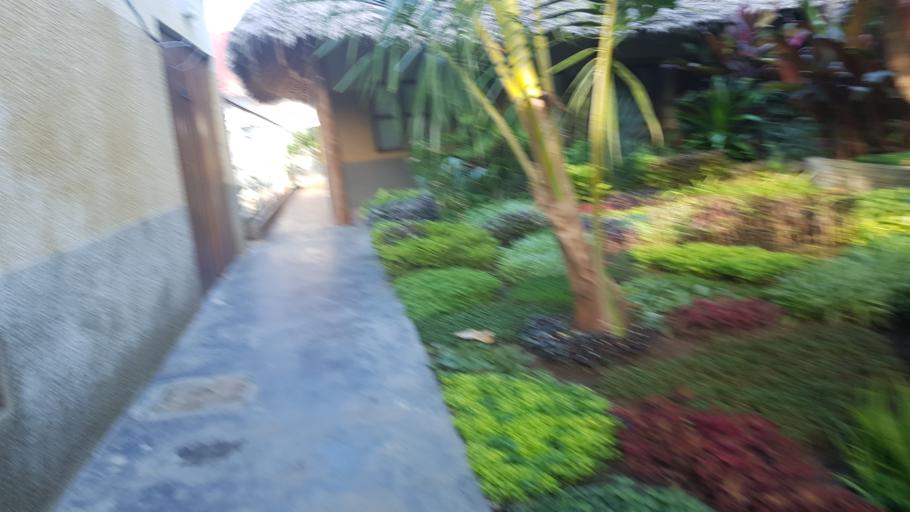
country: TZ
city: Kiwengwa
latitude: -6.0350
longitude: 39.4060
